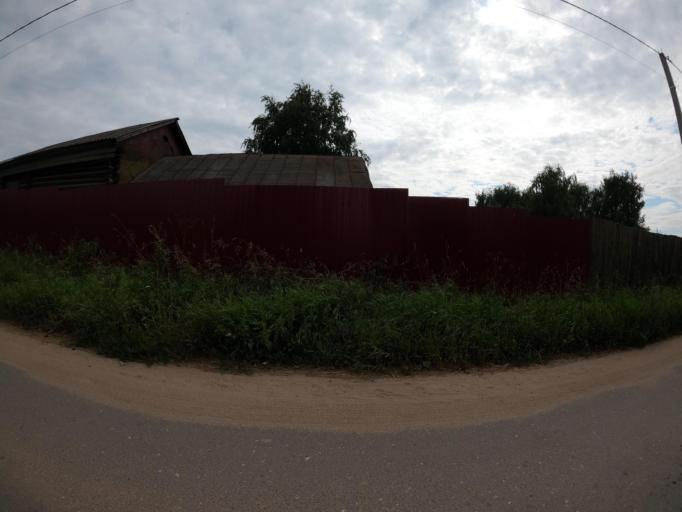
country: RU
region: Moskovskaya
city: Bronnitsy
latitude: 55.4858
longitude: 38.2557
